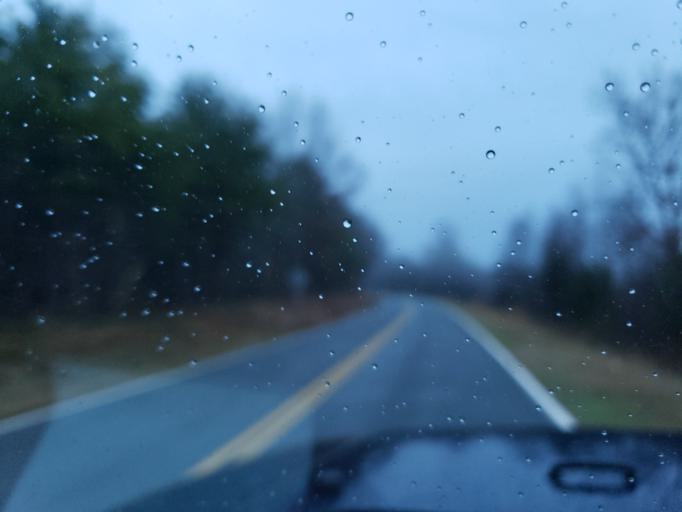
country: US
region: South Carolina
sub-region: Cherokee County
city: Blacksburg
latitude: 35.1413
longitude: -81.4486
